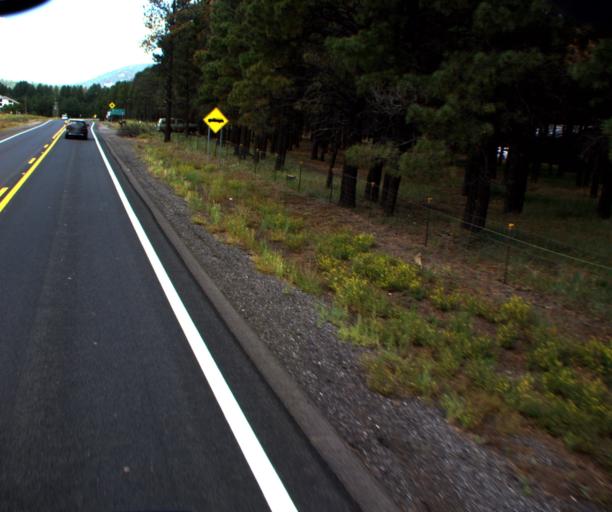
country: US
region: Arizona
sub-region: Coconino County
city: Flagstaff
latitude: 35.2680
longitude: -111.7336
